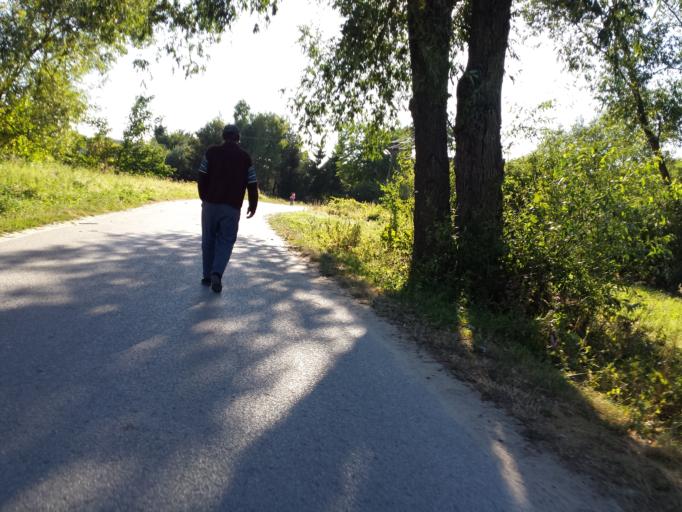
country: PL
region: Swietokrzyskie
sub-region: Powiat kielecki
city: Pierzchnica
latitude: 50.6573
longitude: 20.7915
